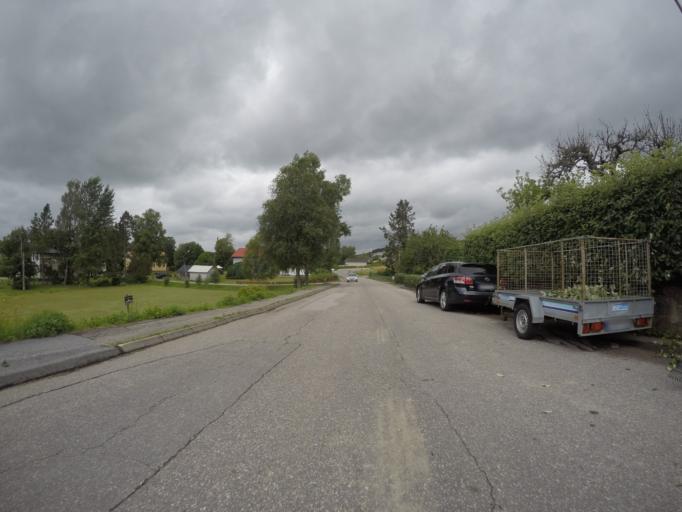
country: SE
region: Vaestra Goetaland
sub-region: Trollhattan
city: Sjuntorp
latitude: 58.1976
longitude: 12.2372
